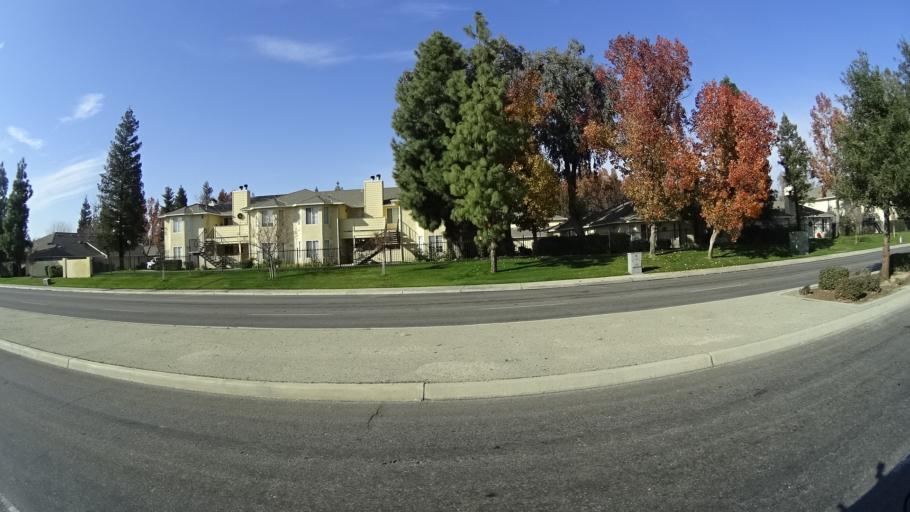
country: US
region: California
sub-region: Kern County
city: Greenacres
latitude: 35.4038
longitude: -119.0743
